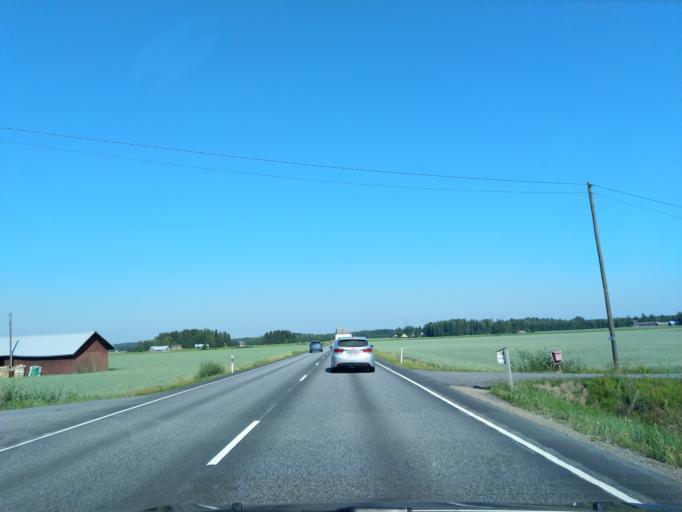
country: FI
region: Varsinais-Suomi
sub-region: Loimaa
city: Alastaro
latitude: 61.0877
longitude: 22.8887
